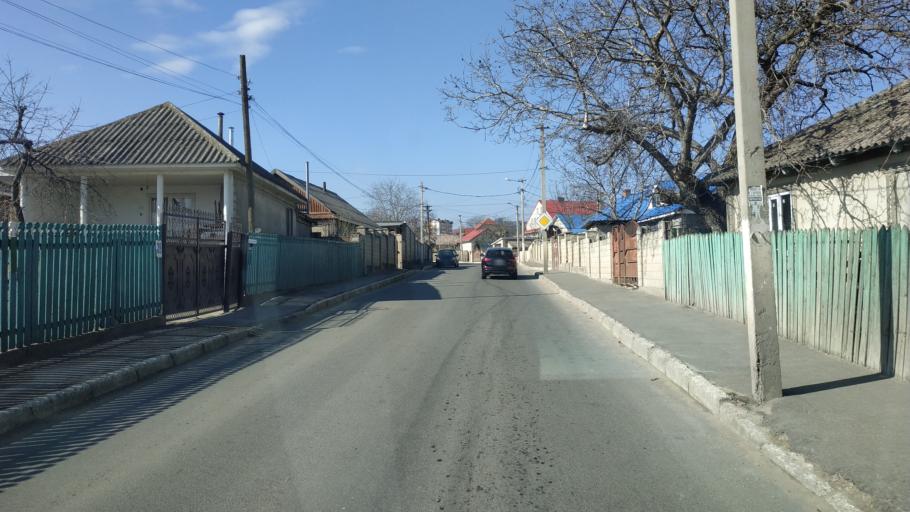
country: MD
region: Chisinau
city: Vatra
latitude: 47.0192
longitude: 28.7580
